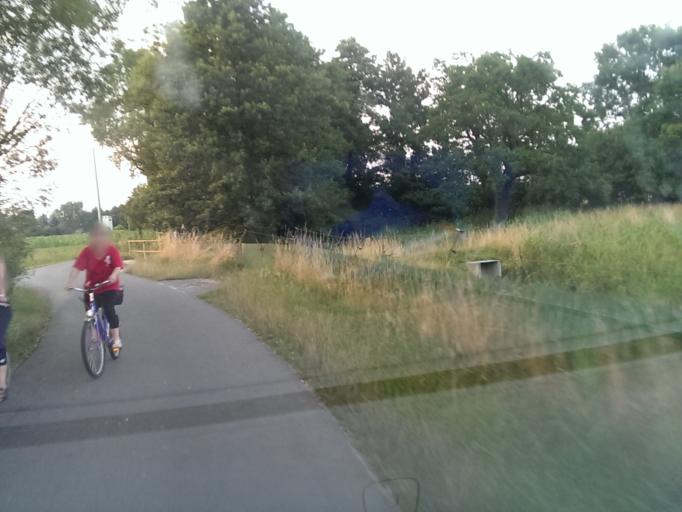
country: DE
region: Brandenburg
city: Golssen
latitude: 51.9626
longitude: 13.6139
